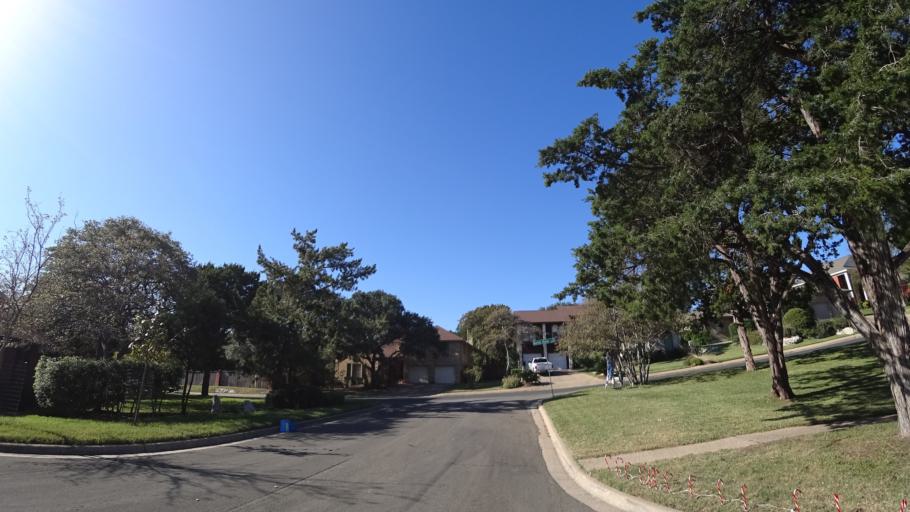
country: US
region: Texas
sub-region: Williamson County
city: Jollyville
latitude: 30.4079
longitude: -97.7553
